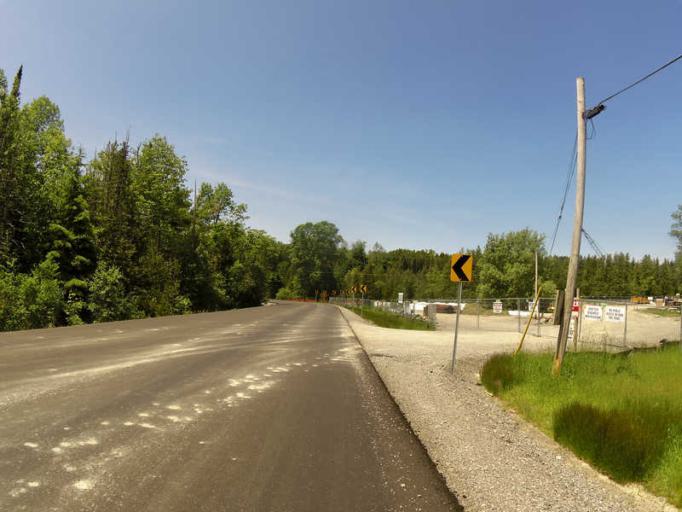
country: CA
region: Ontario
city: Peterborough
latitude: 44.3716
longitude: -78.2878
